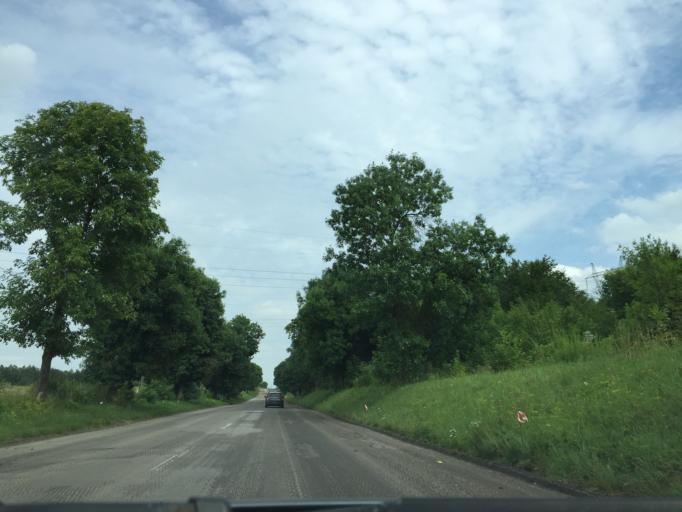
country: PL
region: Silesian Voivodeship
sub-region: Powiat zawiercianski
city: Ogrodzieniec
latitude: 50.4538
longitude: 19.5358
